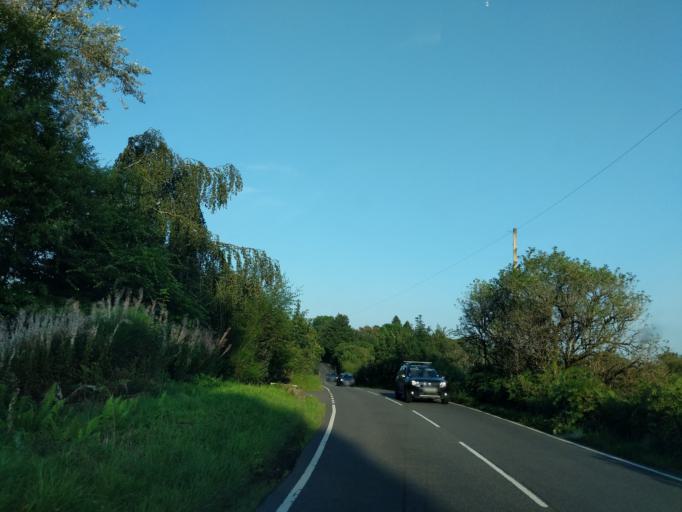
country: GB
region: Scotland
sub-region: Stirling
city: Balfron
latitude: 56.1780
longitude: -4.3206
